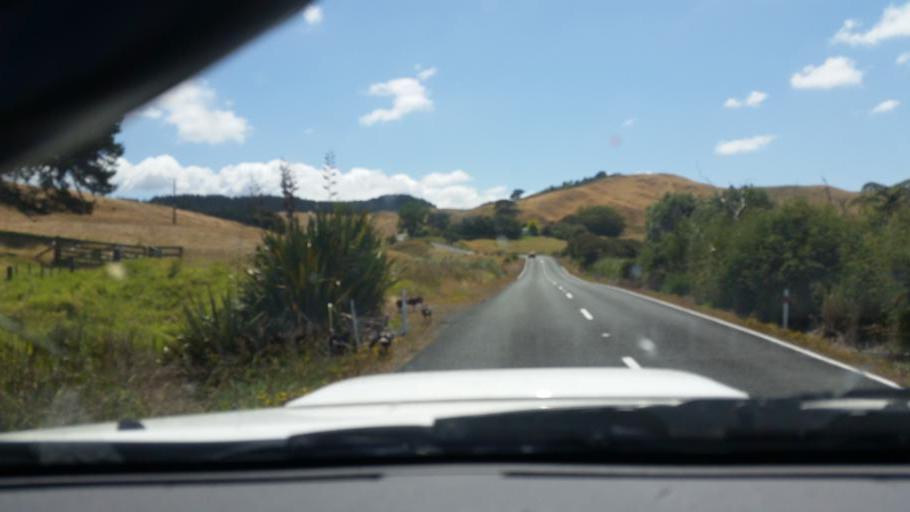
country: NZ
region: Northland
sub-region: Kaipara District
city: Dargaville
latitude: -35.8257
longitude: 173.6763
